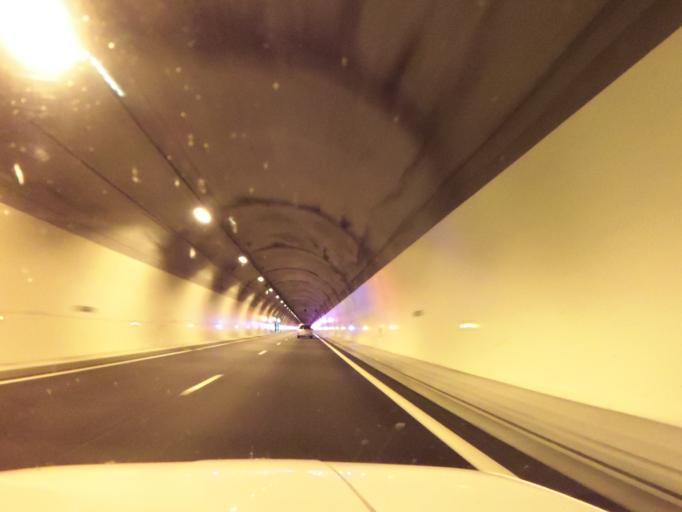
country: FR
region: Rhone-Alpes
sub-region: Departement de la Loire
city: Violay
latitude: 45.8623
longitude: 4.3707
